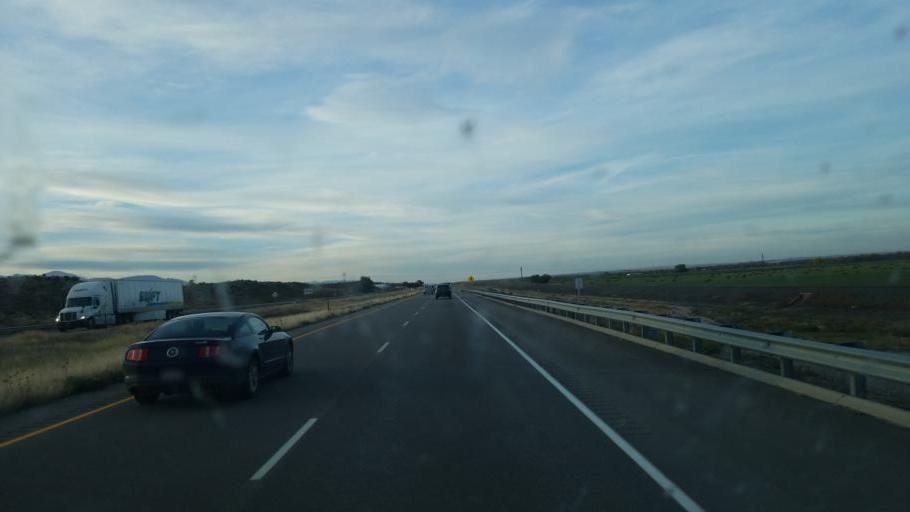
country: US
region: Colorado
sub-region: El Paso County
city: Fountain
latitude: 38.5522
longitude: -104.6474
